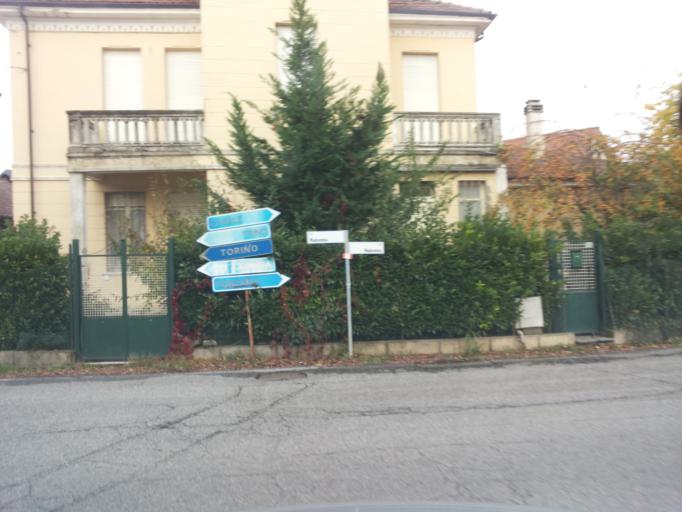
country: IT
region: Piedmont
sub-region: Provincia di Alessandria
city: Cereseto
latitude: 45.1026
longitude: 8.3072
